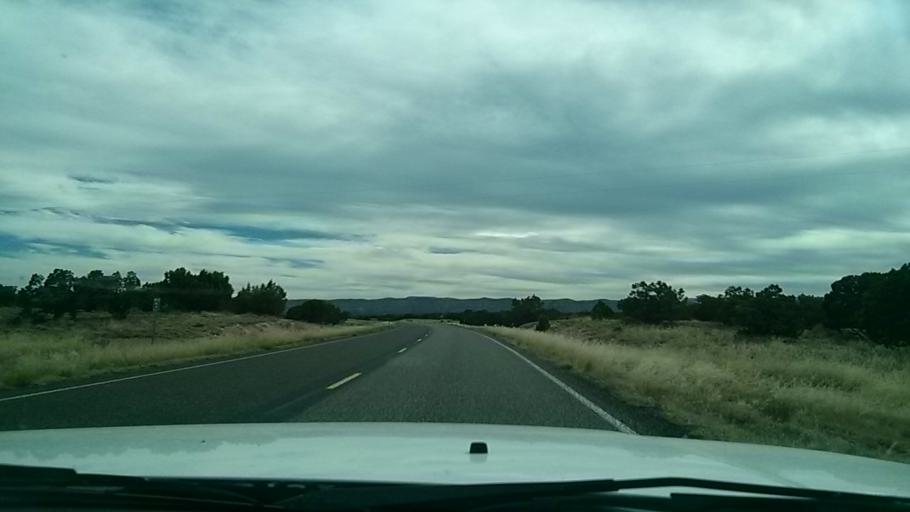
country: US
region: Utah
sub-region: Wayne County
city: Loa
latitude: 37.7483
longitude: -111.4916
